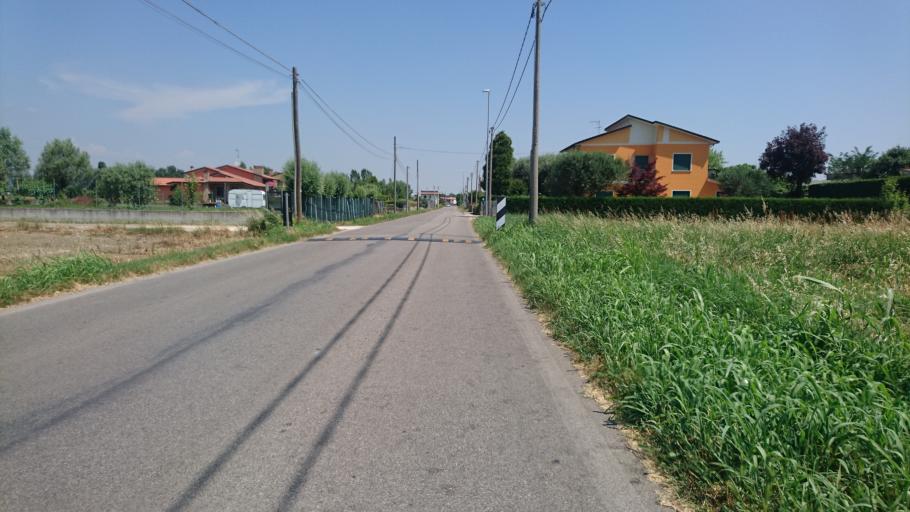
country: IT
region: Veneto
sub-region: Provincia di Padova
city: Solesino
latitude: 45.1682
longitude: 11.7379
